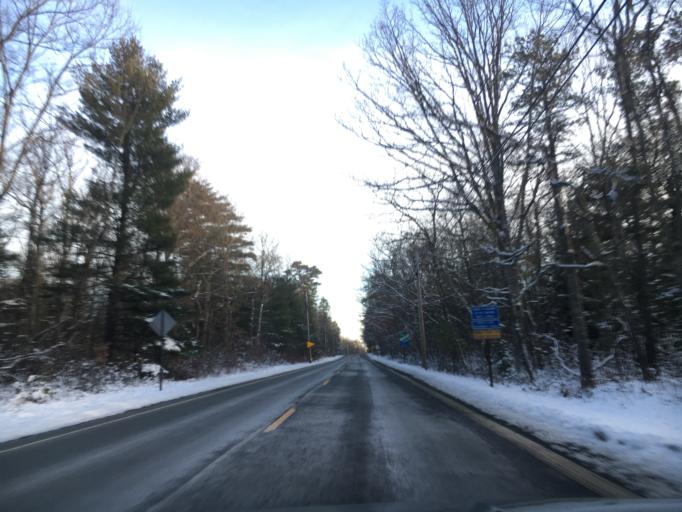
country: US
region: Pennsylvania
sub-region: Pike County
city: Hemlock Farms
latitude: 41.3032
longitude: -75.1009
